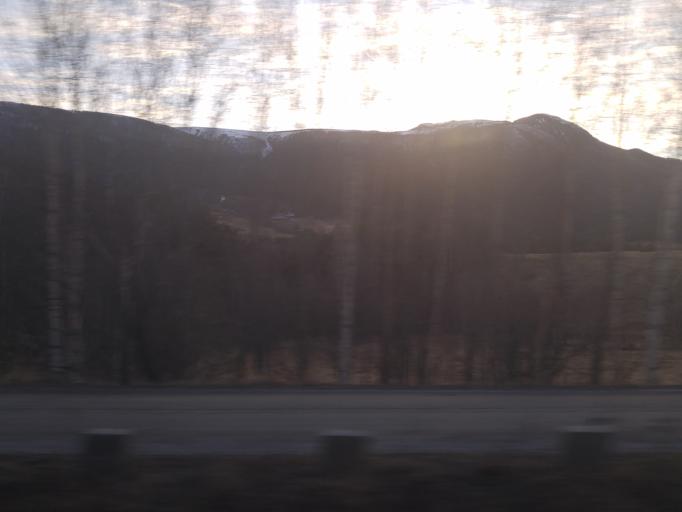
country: NO
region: Oppland
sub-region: Dovre
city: Dovre
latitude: 61.9816
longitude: 9.2575
